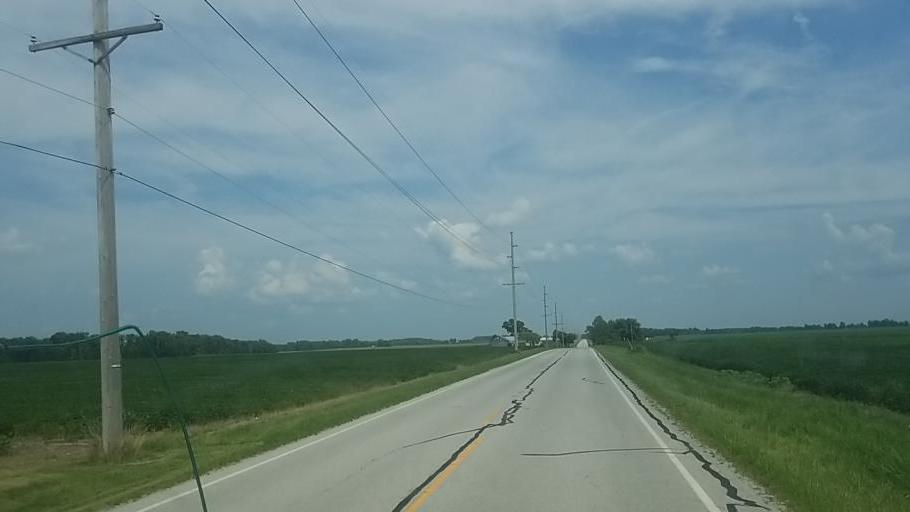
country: US
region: Ohio
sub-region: Hardin County
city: Forest
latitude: 40.7820
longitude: -83.5603
